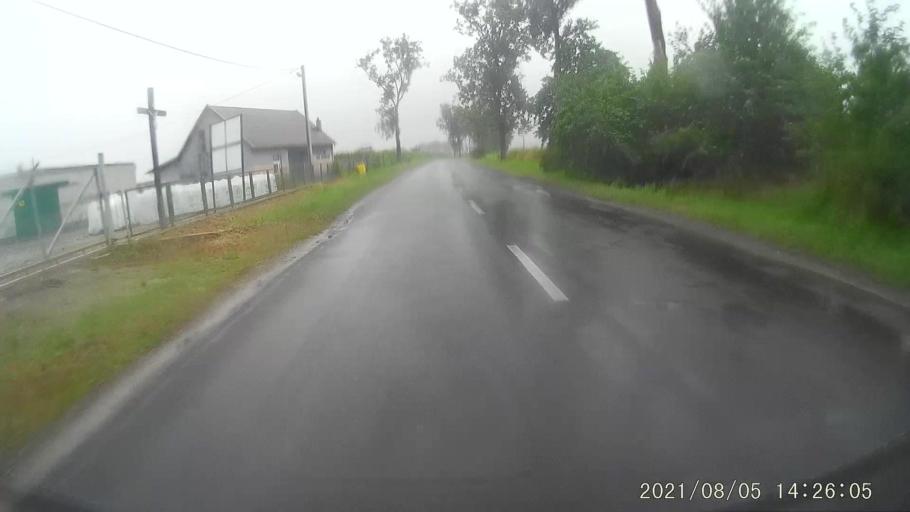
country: PL
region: Opole Voivodeship
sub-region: Powiat nyski
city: Korfantow
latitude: 50.4867
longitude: 17.6060
